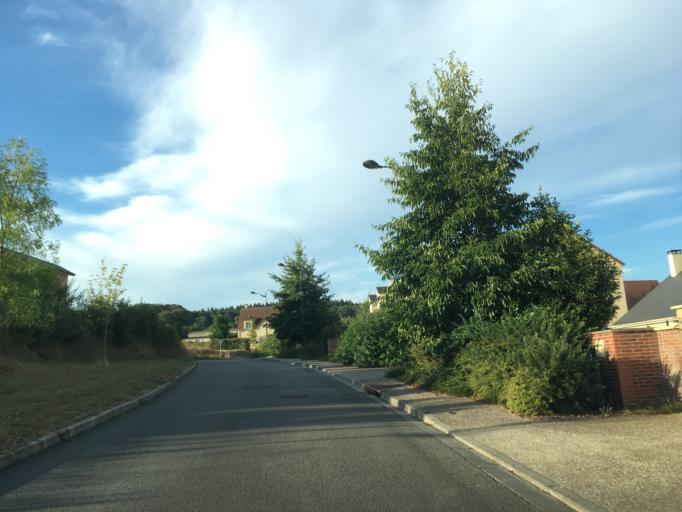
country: FR
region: Haute-Normandie
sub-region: Departement de l'Eure
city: Vernon
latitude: 49.0791
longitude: 1.4978
